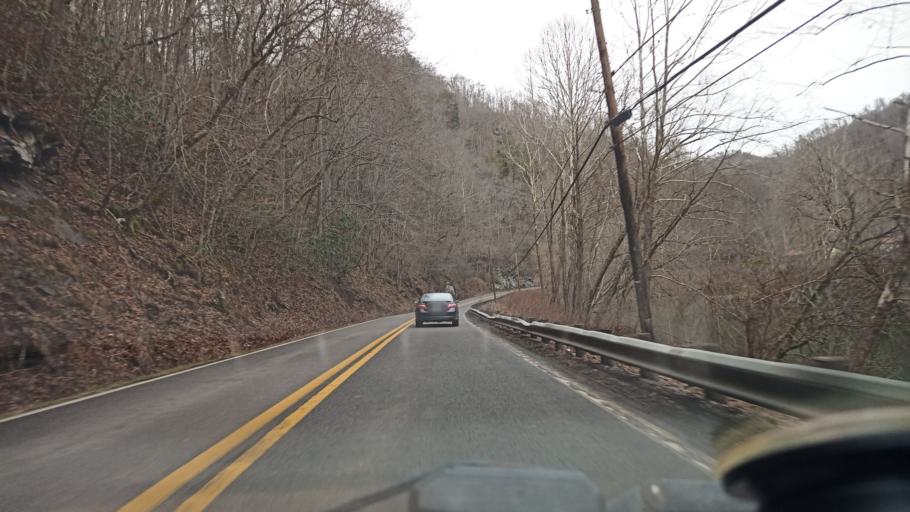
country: US
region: West Virginia
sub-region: Logan County
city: Mallory
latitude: 37.6614
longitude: -81.8655
